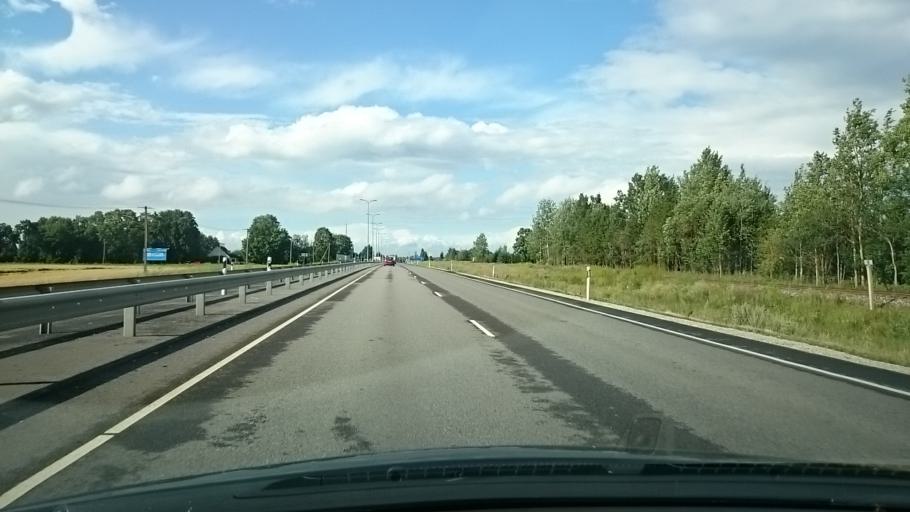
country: EE
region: Tartu
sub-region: UElenurme vald
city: Ulenurme
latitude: 58.3309
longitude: 26.7149
